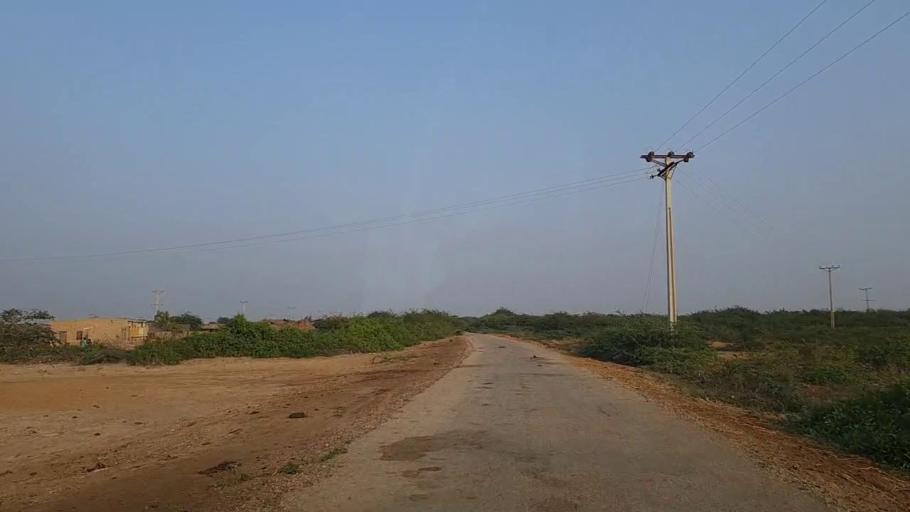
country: PK
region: Sindh
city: Thatta
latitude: 24.6900
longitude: 67.8153
